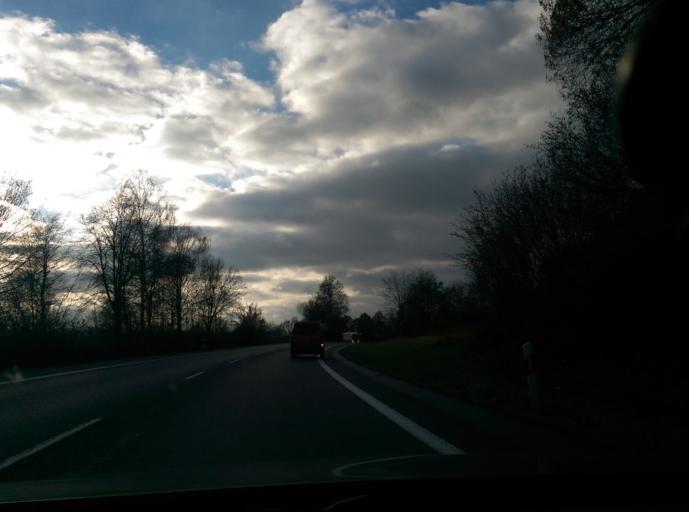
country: DE
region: Hesse
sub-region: Regierungsbezirk Kassel
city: Eschwege
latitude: 51.2080
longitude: 9.9991
